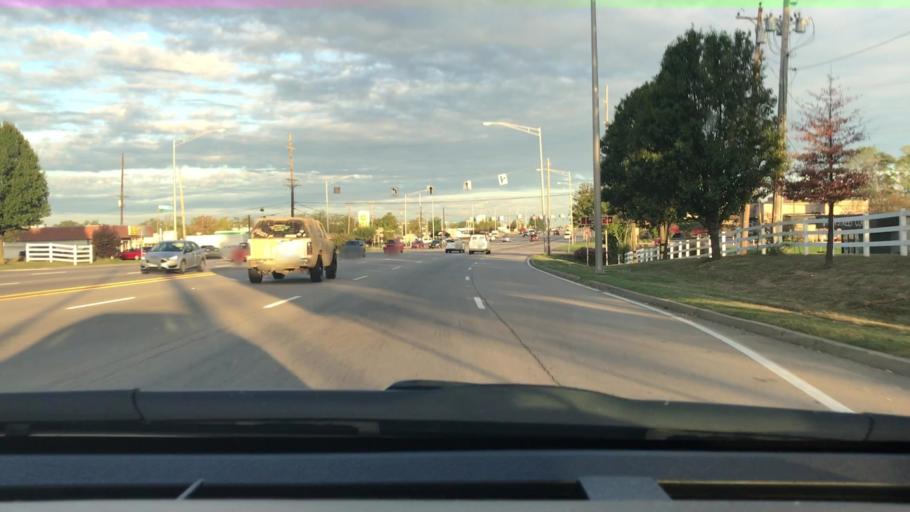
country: US
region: Kentucky
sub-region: Boone County
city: Florence
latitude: 39.0020
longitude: -84.6497
